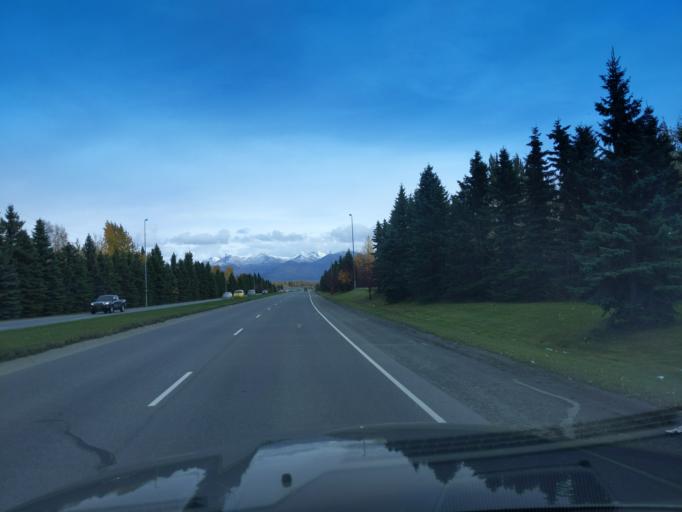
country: US
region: Alaska
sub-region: Anchorage Municipality
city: Anchorage
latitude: 61.1735
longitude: -149.9390
